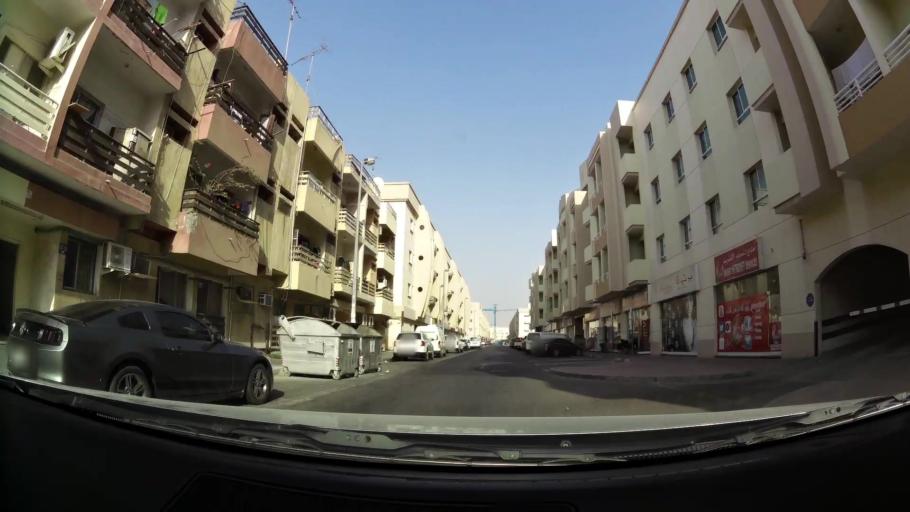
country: AE
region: Ash Shariqah
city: Sharjah
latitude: 25.2422
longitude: 55.2998
